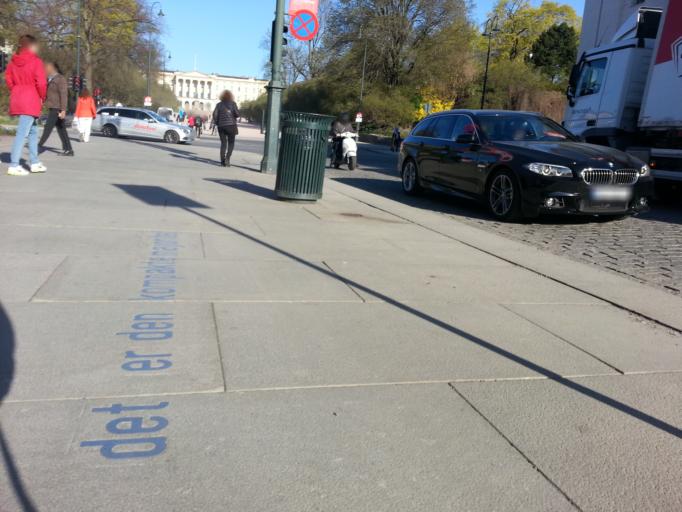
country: NO
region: Oslo
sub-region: Oslo
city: Oslo
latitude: 59.9151
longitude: 10.7337
